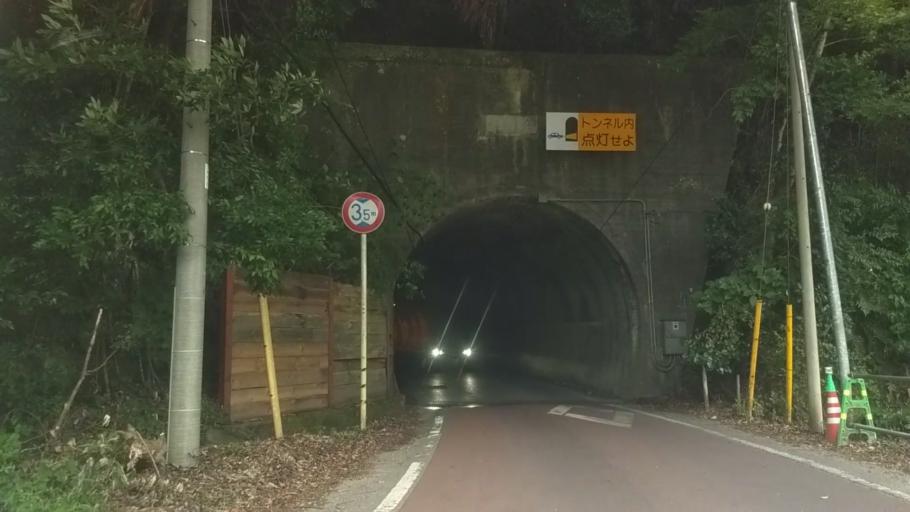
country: JP
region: Chiba
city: Kawaguchi
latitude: 35.2286
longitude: 140.1279
